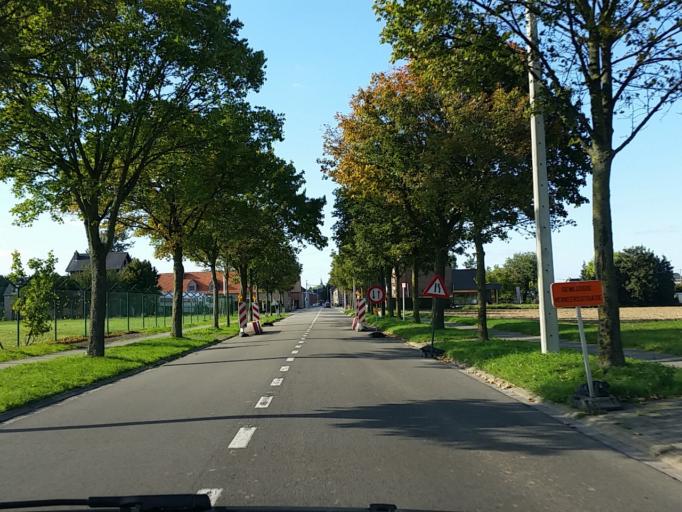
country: BE
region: Flanders
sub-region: Provincie Vlaams-Brabant
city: Kortenberg
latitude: 50.9012
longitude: 4.5242
